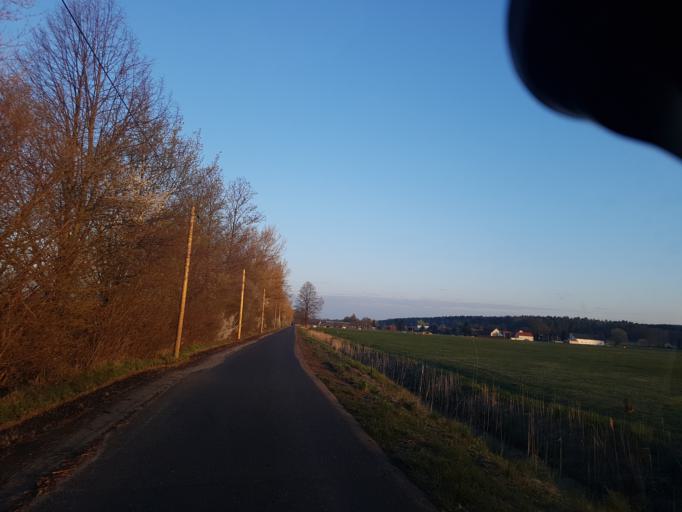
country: DE
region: Brandenburg
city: Falkenberg
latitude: 51.6352
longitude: 13.3055
